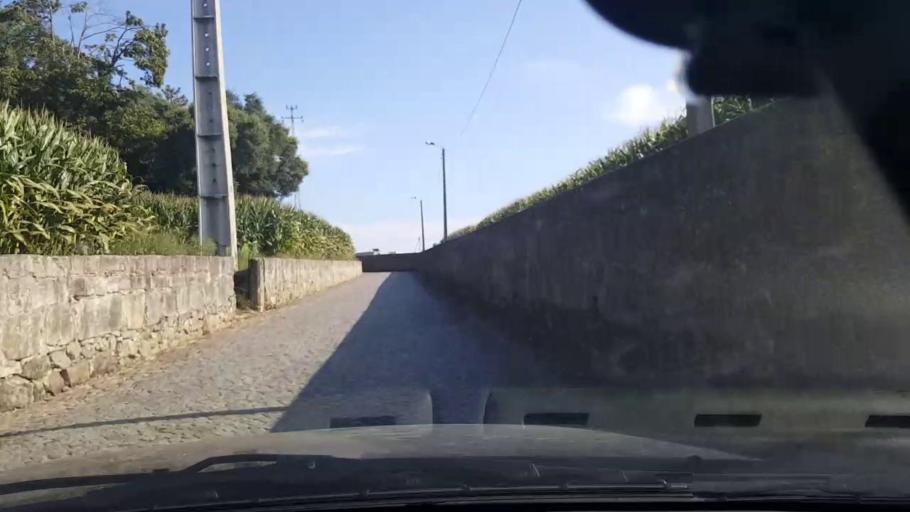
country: PT
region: Porto
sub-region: Maia
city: Gemunde
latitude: 41.2750
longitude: -8.6691
